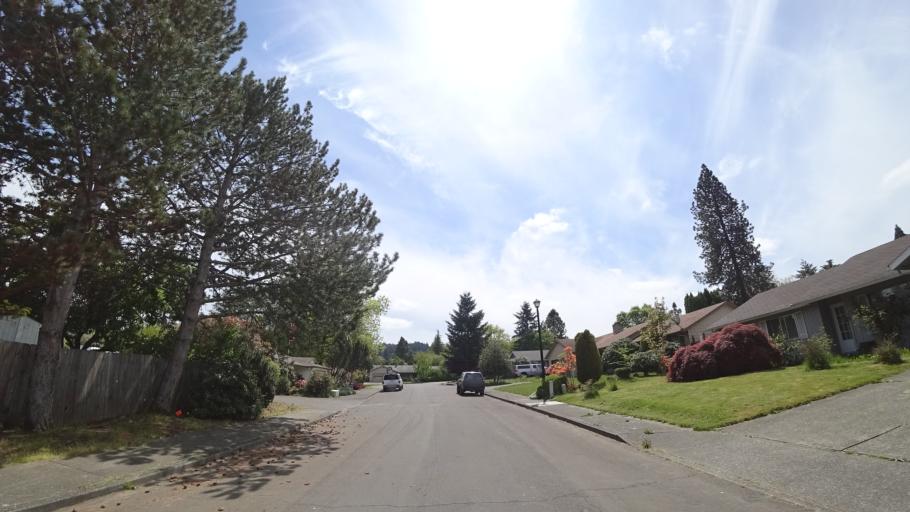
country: US
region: Oregon
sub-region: Washington County
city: Aloha
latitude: 45.4719
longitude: -122.8830
